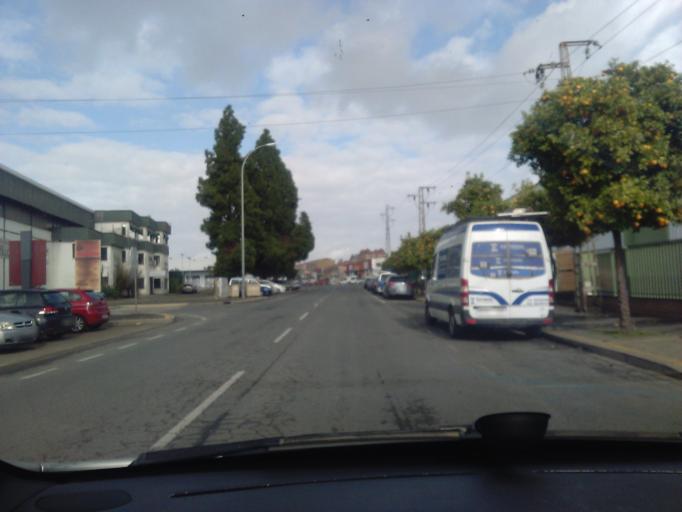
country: ES
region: Andalusia
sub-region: Provincia de Sevilla
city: Sevilla
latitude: 37.3808
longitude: -5.9245
